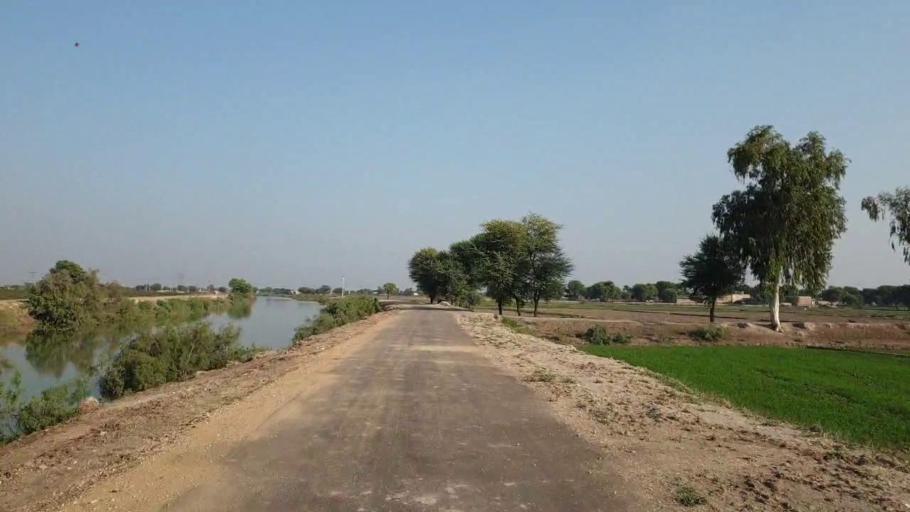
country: PK
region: Sindh
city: Sehwan
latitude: 26.4370
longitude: 67.7899
